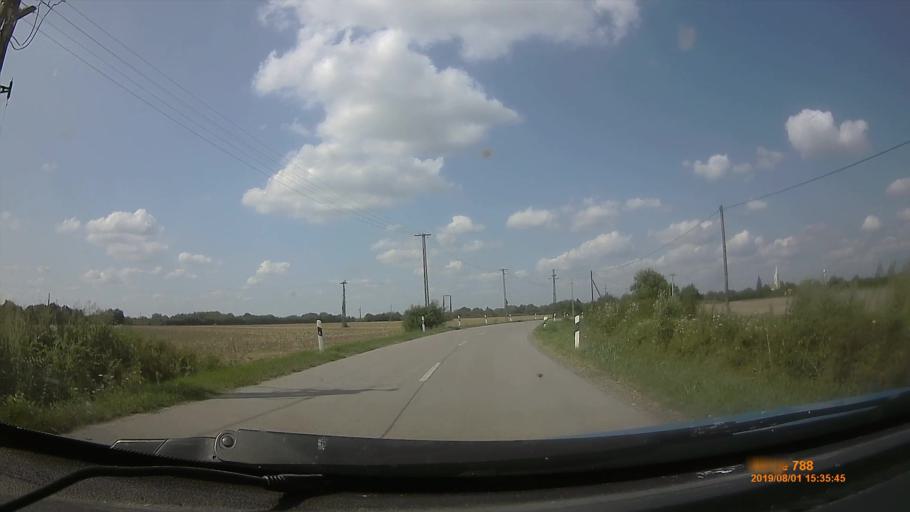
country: HU
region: Baranya
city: Szentlorinc
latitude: 45.9624
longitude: 17.9130
